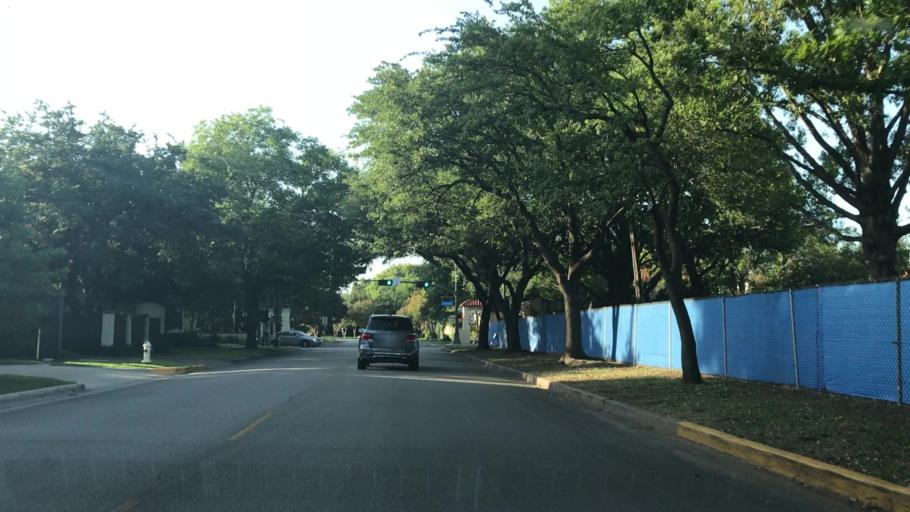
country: US
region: Texas
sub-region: Dallas County
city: University Park
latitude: 32.8359
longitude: -96.8104
